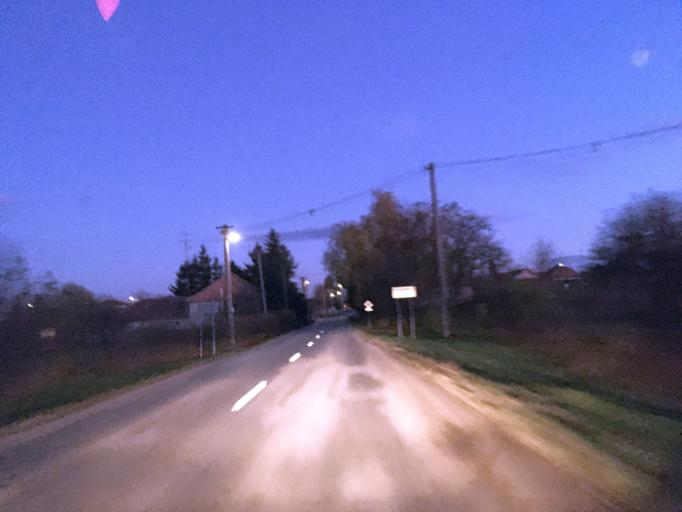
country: SK
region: Nitriansky
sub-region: Okres Komarno
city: Hurbanovo
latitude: 47.8905
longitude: 18.1971
